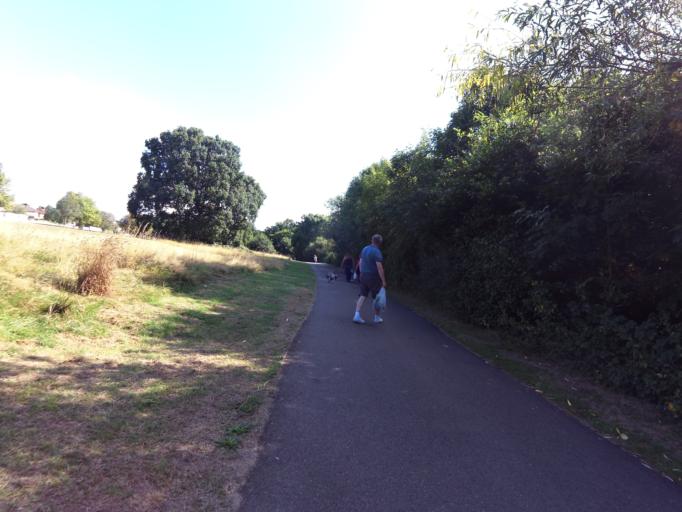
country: GB
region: England
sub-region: Greater London
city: Wood Green
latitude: 51.6300
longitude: -0.1438
